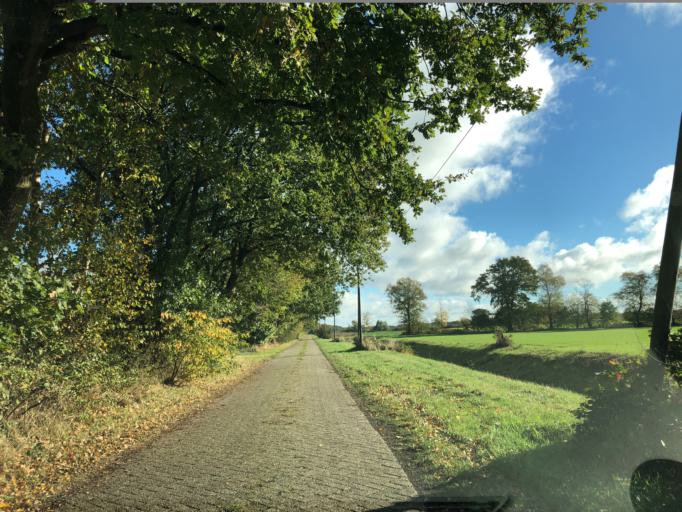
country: DE
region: Lower Saxony
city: Lehe
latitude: 53.0358
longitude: 7.3521
